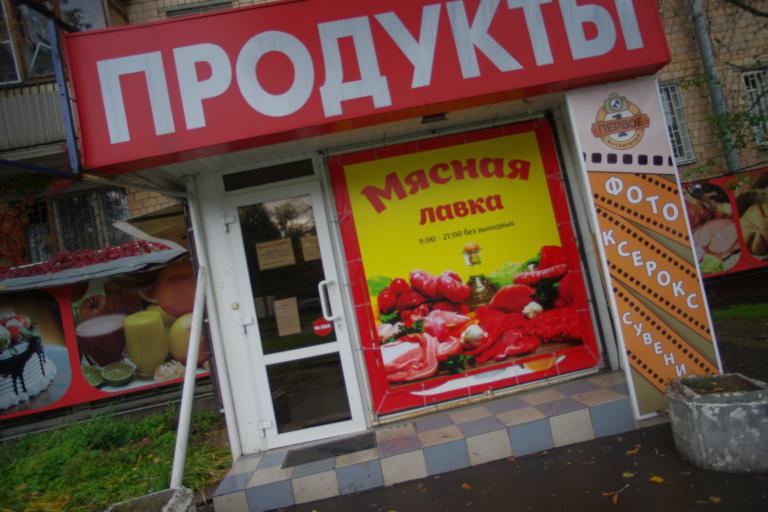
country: RU
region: Moscow
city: Novyye Cheremushki
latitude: 55.6915
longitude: 37.5750
